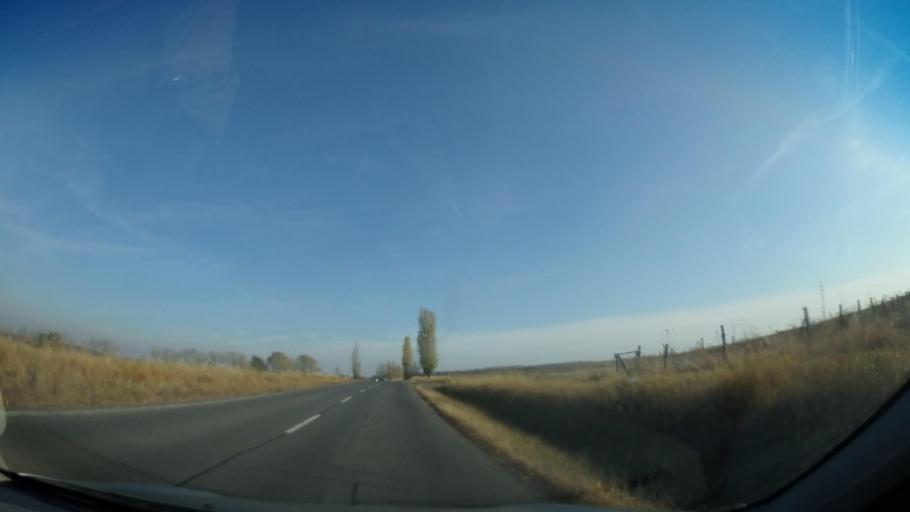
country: CZ
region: Praha
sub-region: Praha 14
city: Dolni Pocernice
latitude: 50.0629
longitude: 14.6098
